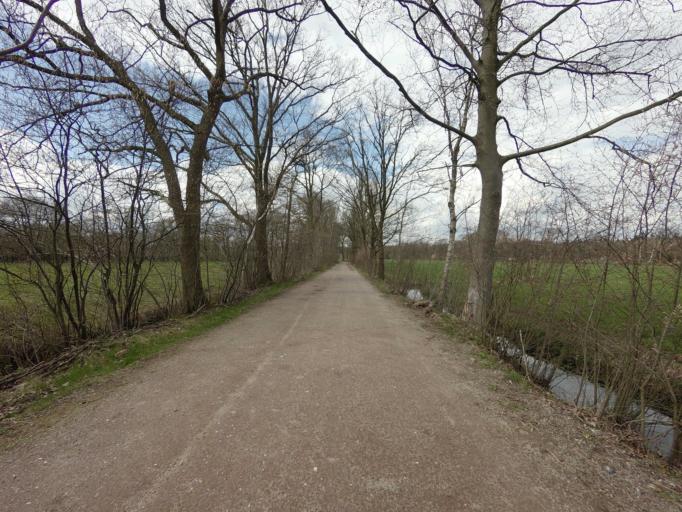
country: NL
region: Utrecht
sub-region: Gemeente Soest
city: Soest
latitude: 52.1675
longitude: 5.2506
